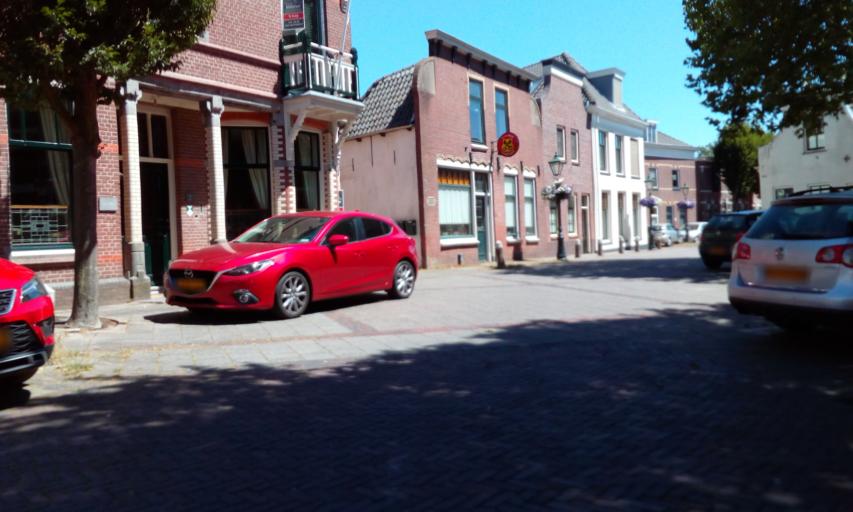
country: NL
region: South Holland
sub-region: Bodegraven-Reeuwijk
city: Bodegraven
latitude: 52.1060
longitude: 4.7280
